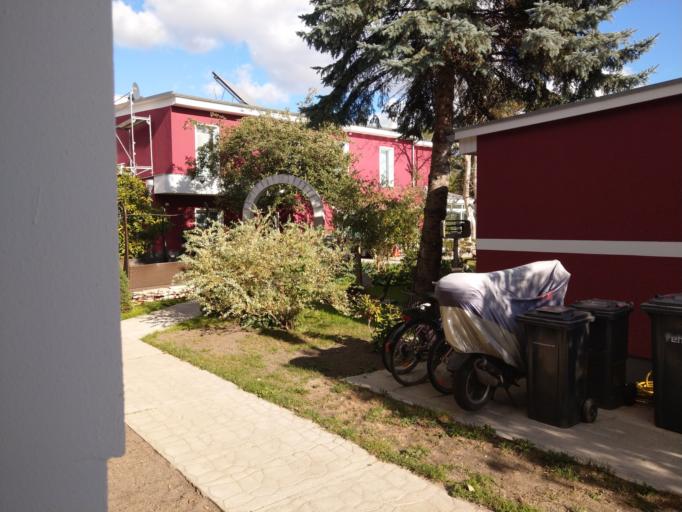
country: DE
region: Brandenburg
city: Bernau bei Berlin
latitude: 52.6795
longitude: 13.5951
